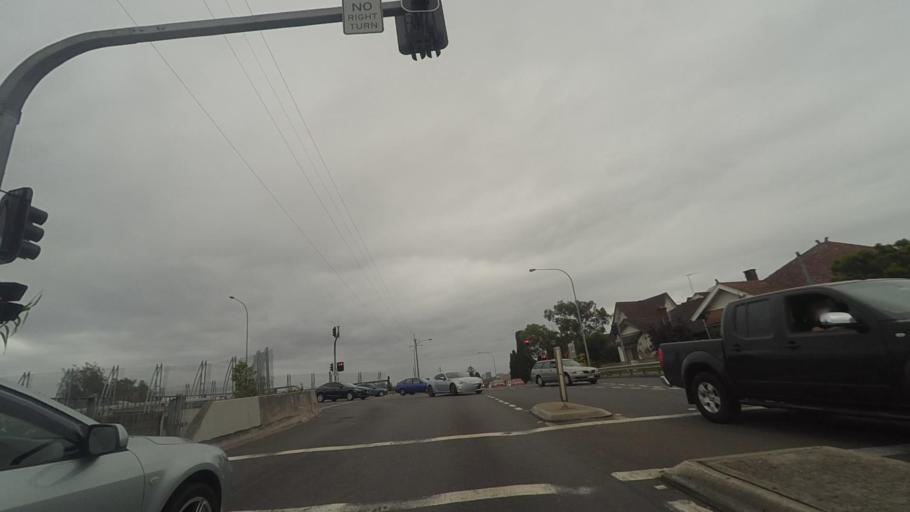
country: AU
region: New South Wales
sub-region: Auburn
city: Auburn
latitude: -33.8473
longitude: 151.0311
